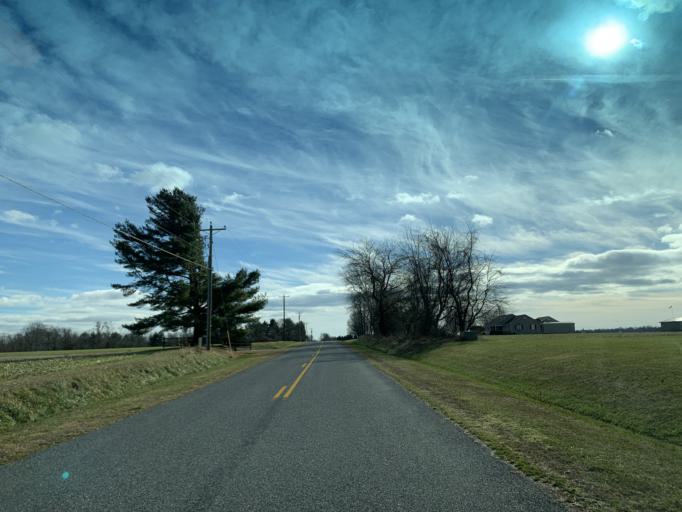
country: US
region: Maryland
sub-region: Kent County
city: Chestertown
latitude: 39.3417
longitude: -76.0510
